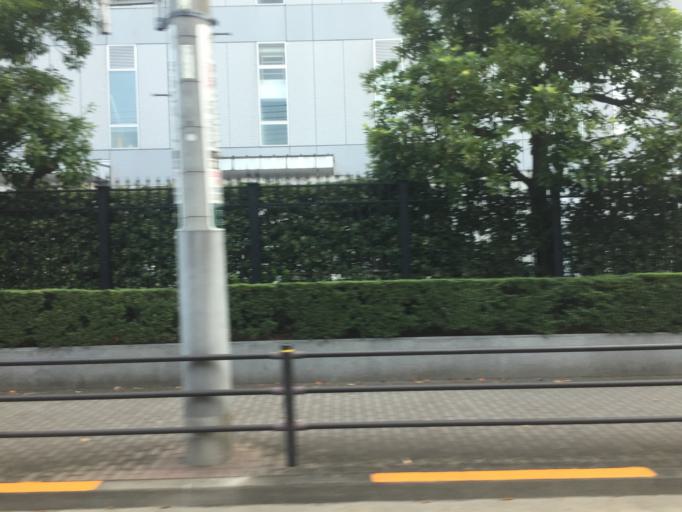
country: JP
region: Kanagawa
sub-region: Kawasaki-shi
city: Kawasaki
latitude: 35.5669
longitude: 139.6839
